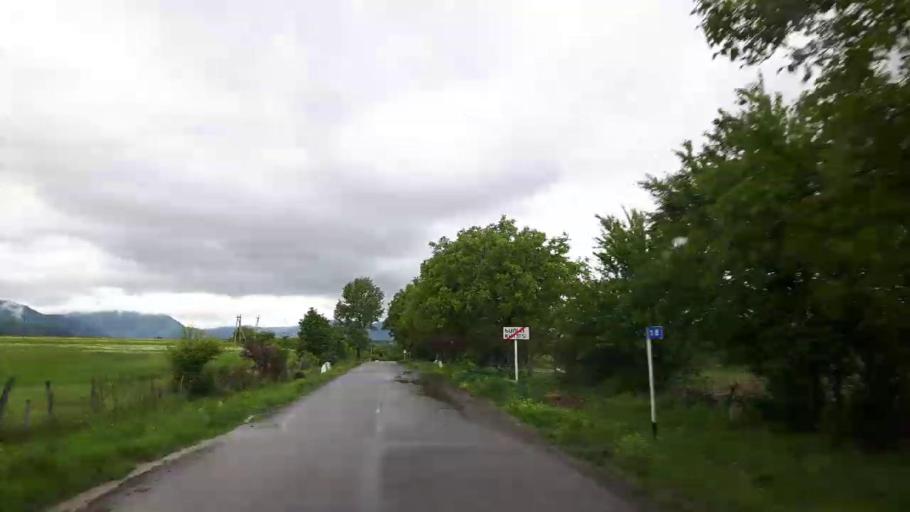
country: GE
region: Shida Kartli
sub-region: Khashuris Raioni
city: Khashuri
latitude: 41.9867
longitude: 43.6619
